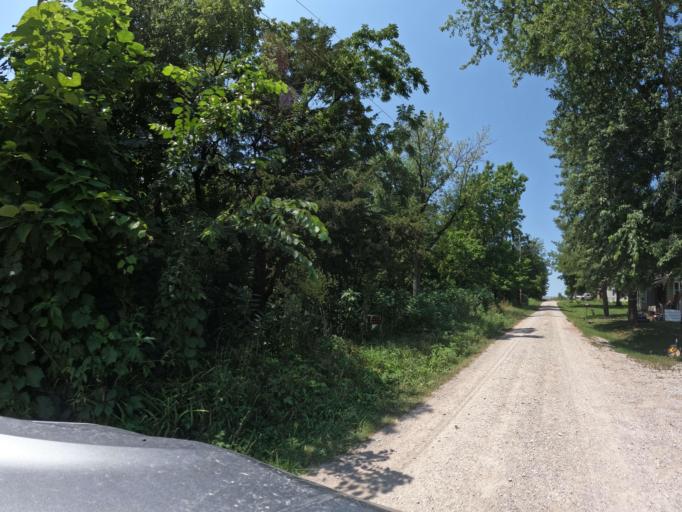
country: US
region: Iowa
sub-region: Appanoose County
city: Centerville
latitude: 40.7741
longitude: -92.9506
